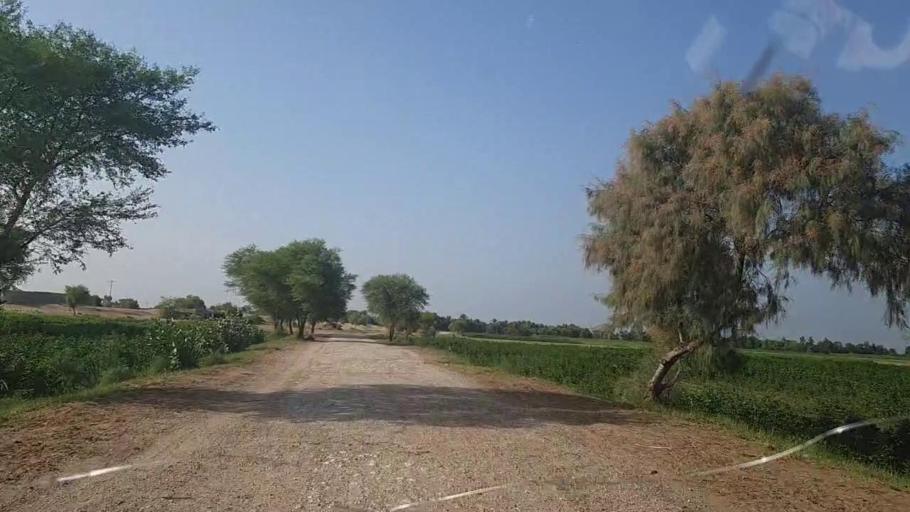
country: PK
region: Sindh
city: Khanpur
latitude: 27.7210
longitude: 69.3318
